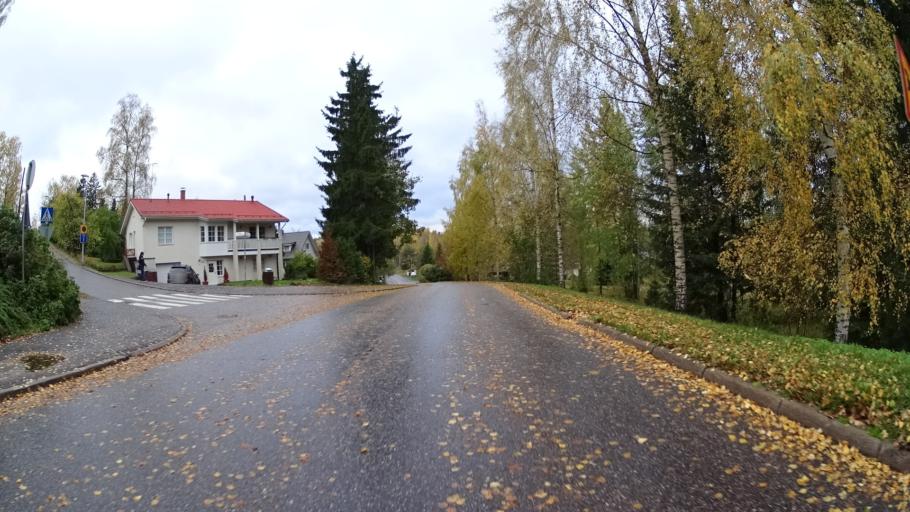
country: FI
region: Uusimaa
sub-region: Helsinki
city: Kilo
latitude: 60.2637
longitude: 24.8218
